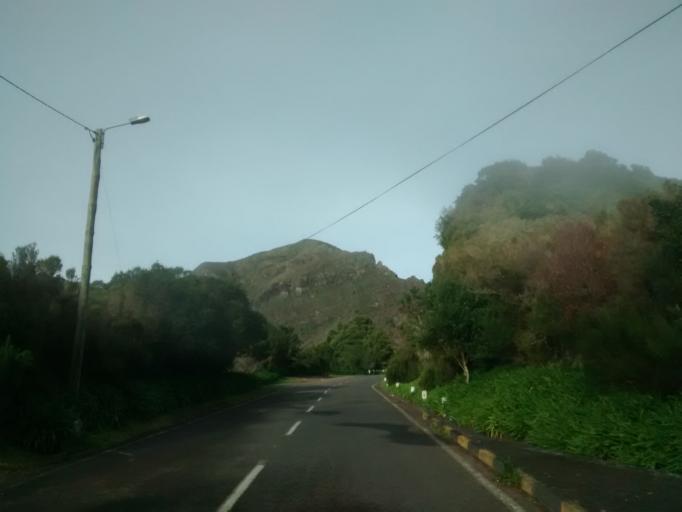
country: PT
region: Madeira
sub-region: Sao Vicente
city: Sao Vicente
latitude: 32.7545
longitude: -17.0202
